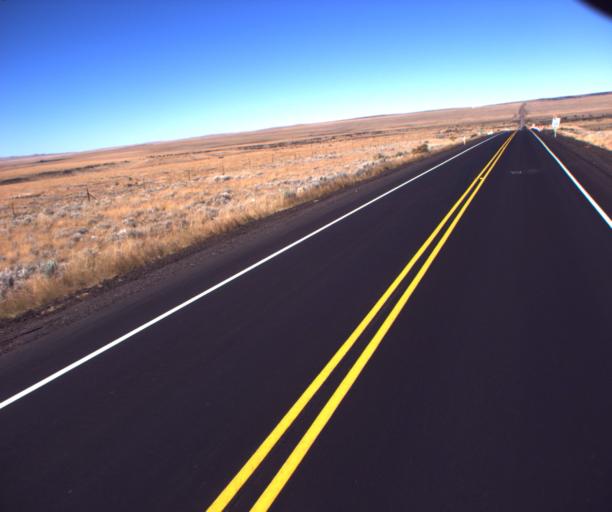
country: US
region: Arizona
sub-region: Apache County
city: Springerville
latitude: 34.2720
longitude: -109.3622
